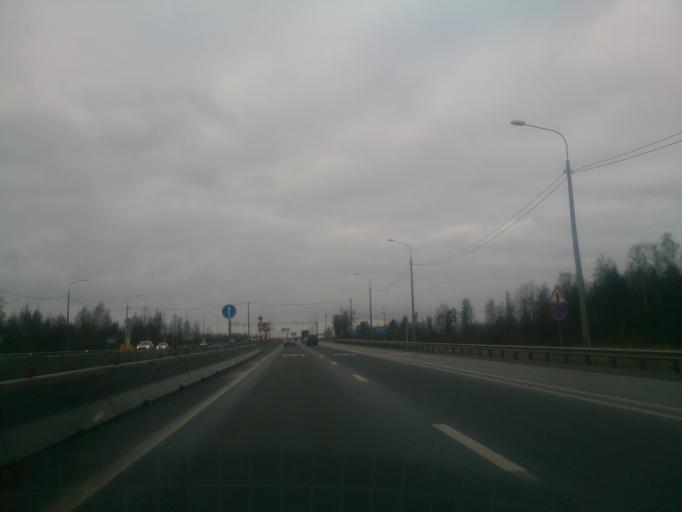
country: RU
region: Leningrad
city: Ul'yanovka
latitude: 59.6074
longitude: 30.7560
